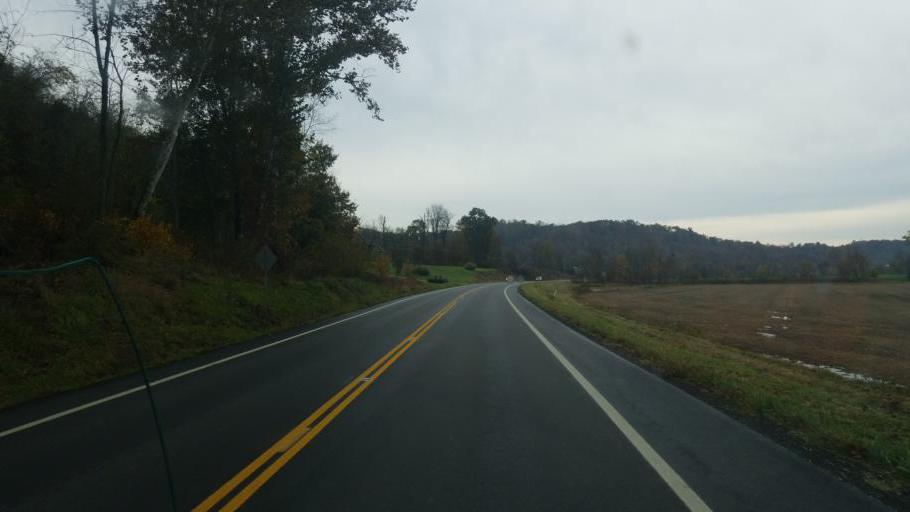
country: US
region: Ohio
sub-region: Washington County
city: Beverly
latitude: 39.5577
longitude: -81.5617
